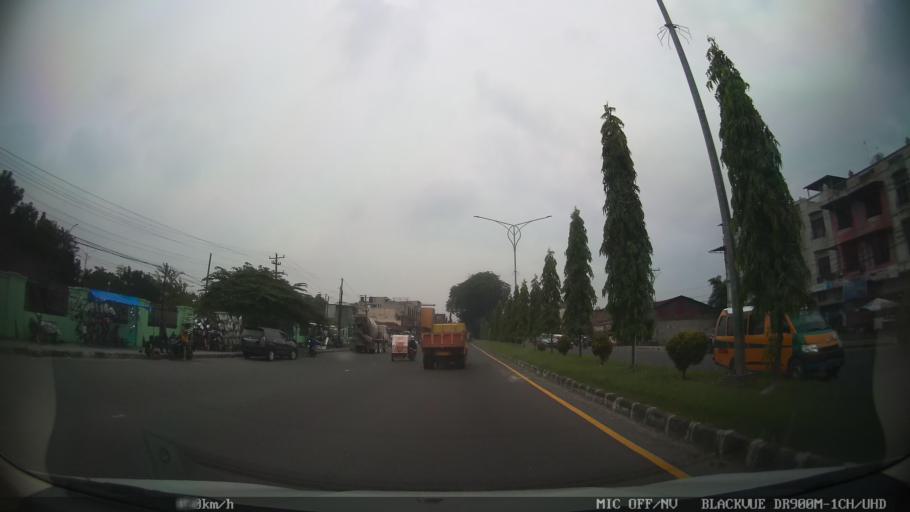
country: ID
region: North Sumatra
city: Deli Tua
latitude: 3.5382
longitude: 98.6867
